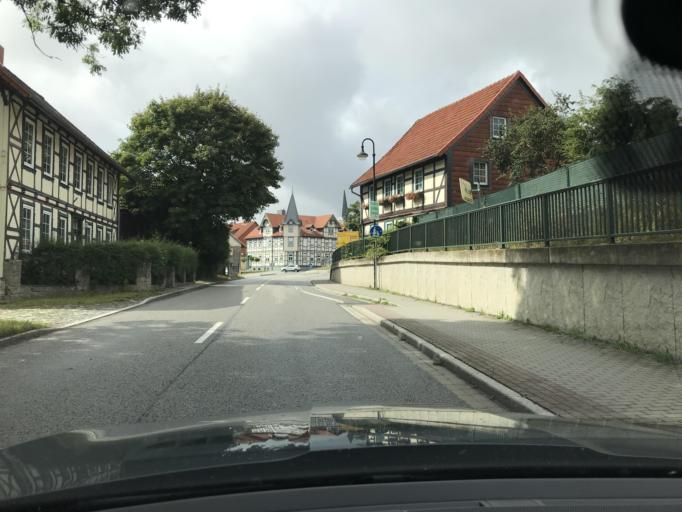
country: DE
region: Saxony-Anhalt
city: Elbingerode
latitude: 51.7694
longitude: 10.8061
